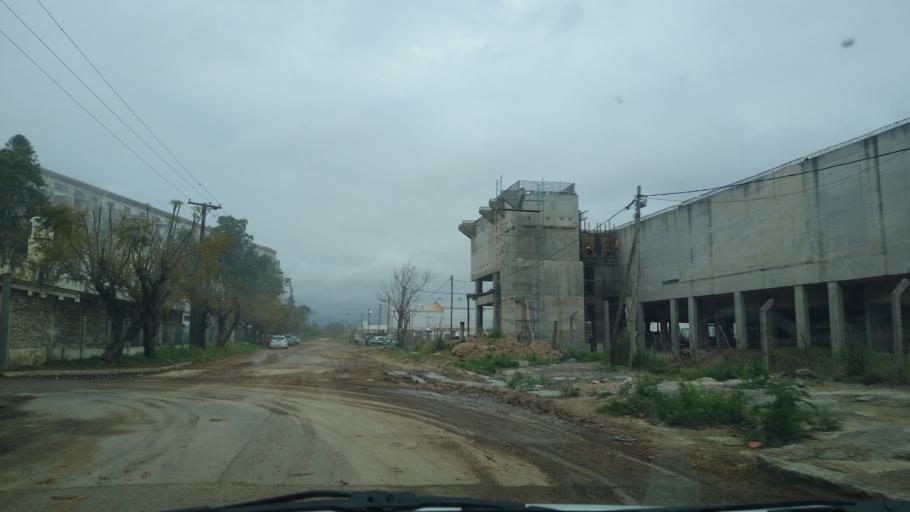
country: AR
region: Chaco
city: Barranqueras
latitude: -27.4719
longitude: -58.9097
